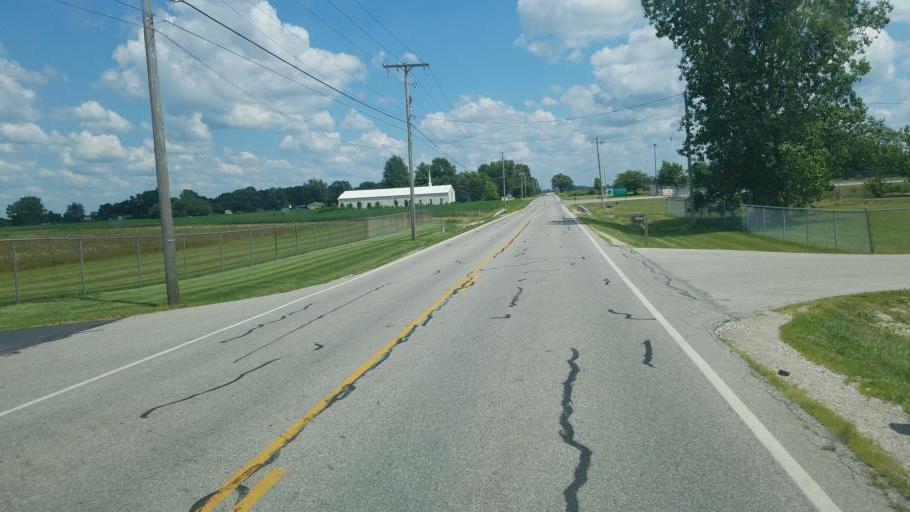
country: US
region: Ohio
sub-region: Marion County
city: Marion
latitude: 40.6151
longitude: -83.0842
